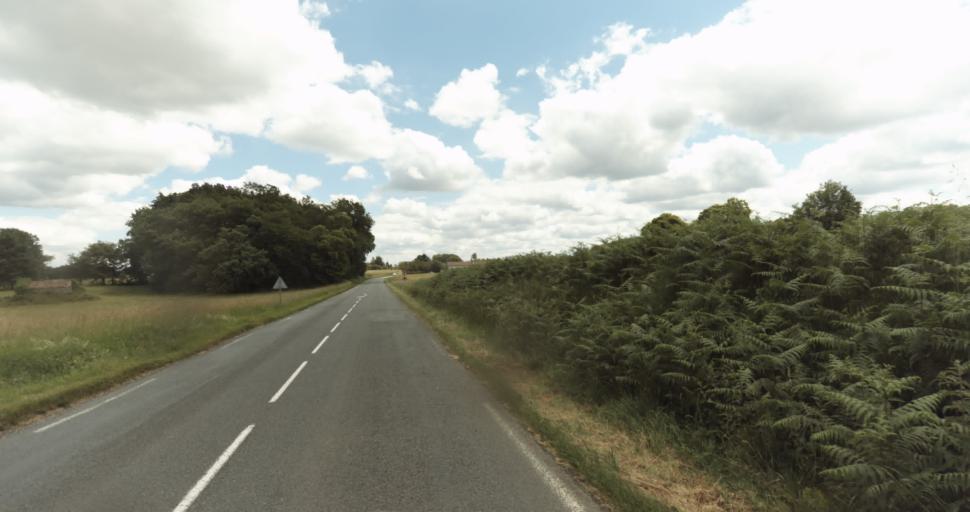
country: FR
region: Aquitaine
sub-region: Departement de la Dordogne
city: Beaumont-du-Perigord
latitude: 44.6930
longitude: 0.8721
